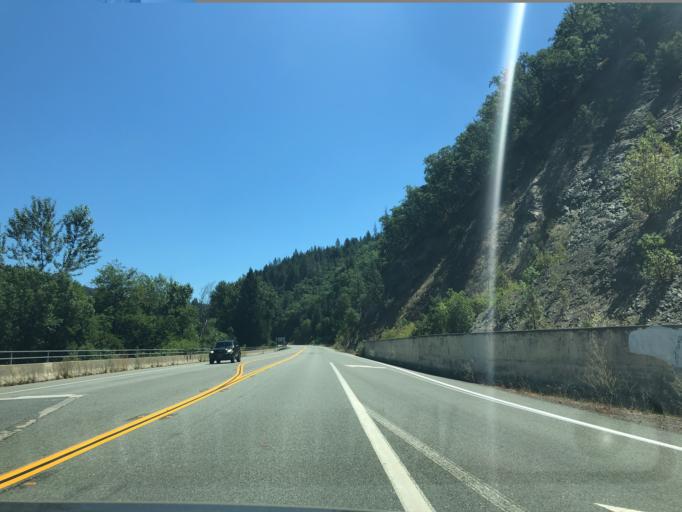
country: US
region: California
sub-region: Trinity County
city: Weaverville
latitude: 40.6514
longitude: -122.9392
